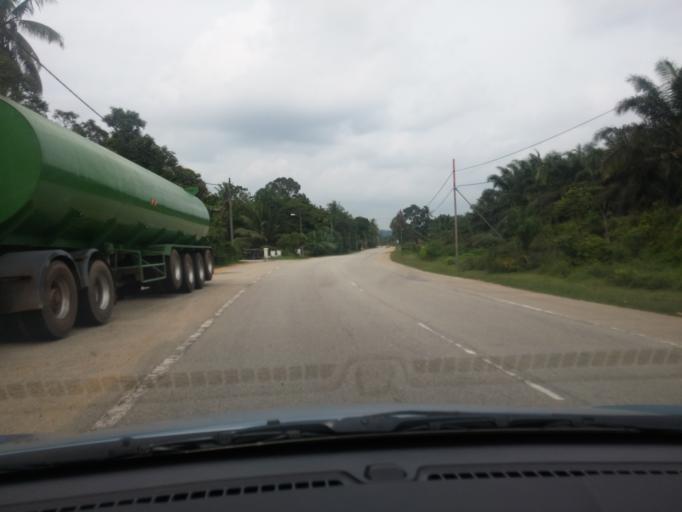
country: MY
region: Pahang
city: Kuantan
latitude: 3.8836
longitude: 103.1646
